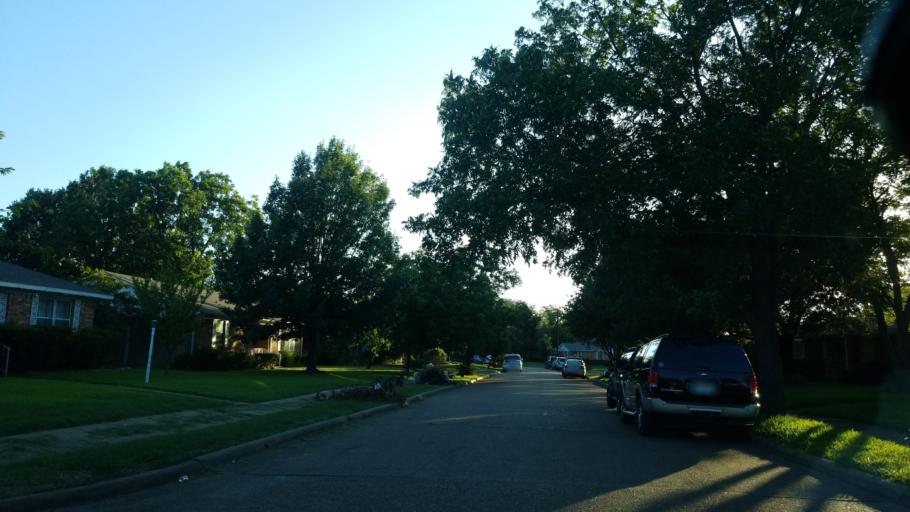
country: US
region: Texas
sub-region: Dallas County
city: Balch Springs
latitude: 32.7907
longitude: -96.6958
